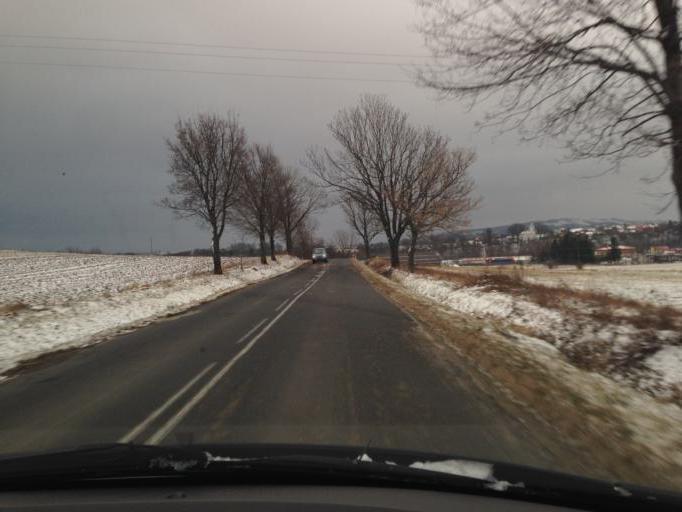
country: PL
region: Subcarpathian Voivodeship
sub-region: Powiat jasielski
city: Nowy Zmigrod
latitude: 49.6090
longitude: 21.5120
